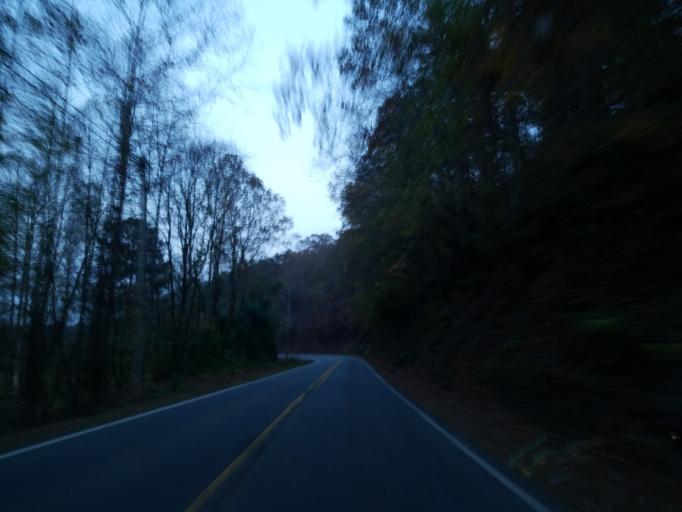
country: US
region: Georgia
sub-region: Pickens County
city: Jasper
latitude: 34.5078
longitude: -84.5046
